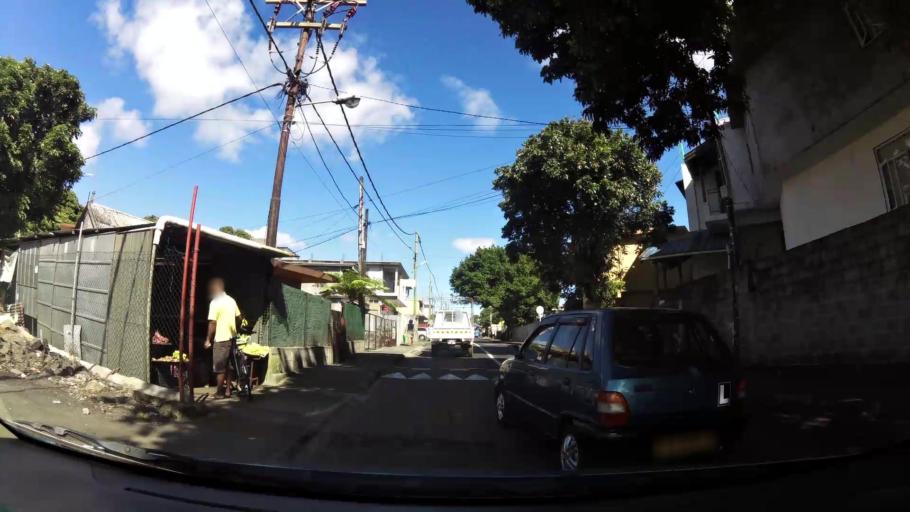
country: MU
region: Plaines Wilhems
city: Vacoas
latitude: -20.3119
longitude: 57.4891
